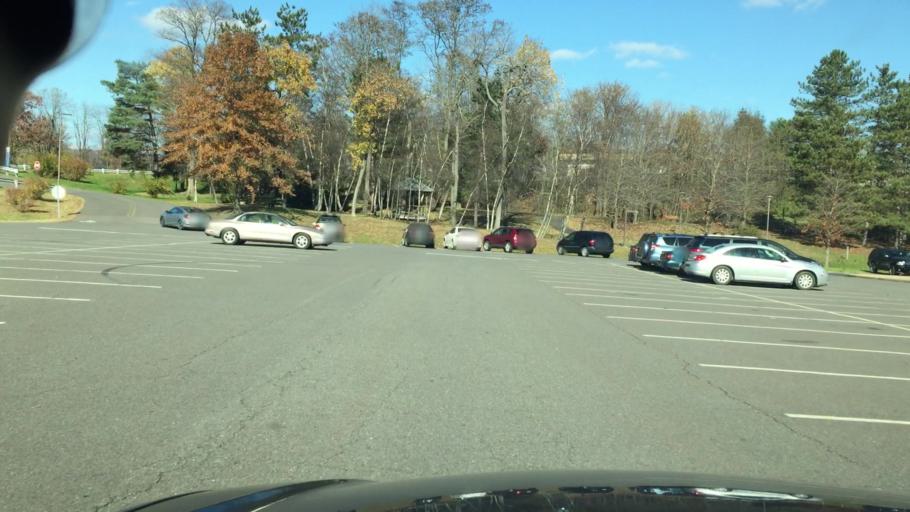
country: US
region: Pennsylvania
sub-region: Luzerne County
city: Nanticoke
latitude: 41.1917
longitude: -75.9947
